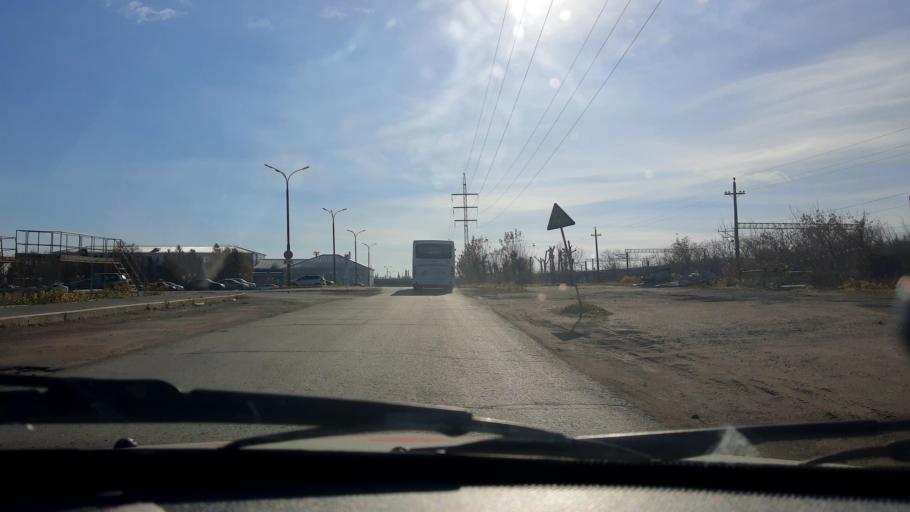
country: RU
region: Bashkortostan
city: Ufa
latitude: 54.8786
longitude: 56.1001
